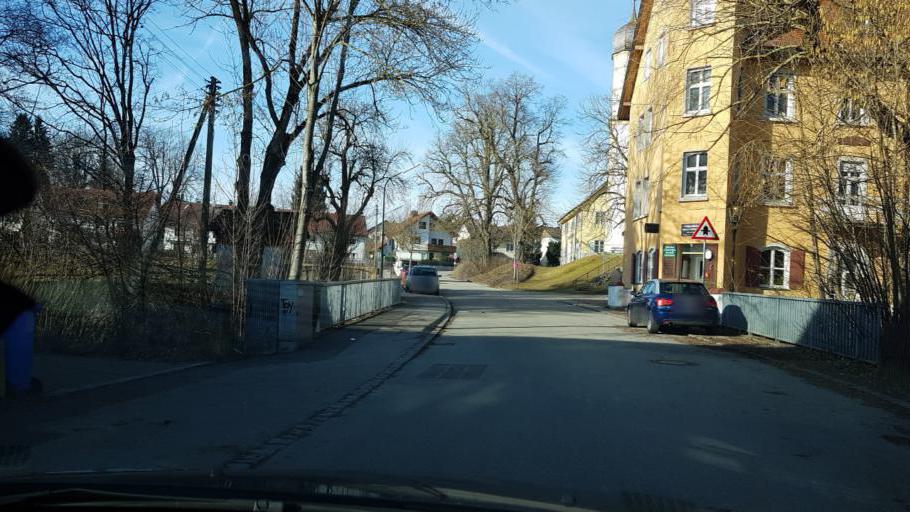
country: DE
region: Bavaria
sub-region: Upper Bavaria
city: Oberschweinbach
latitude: 48.2179
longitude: 11.1737
